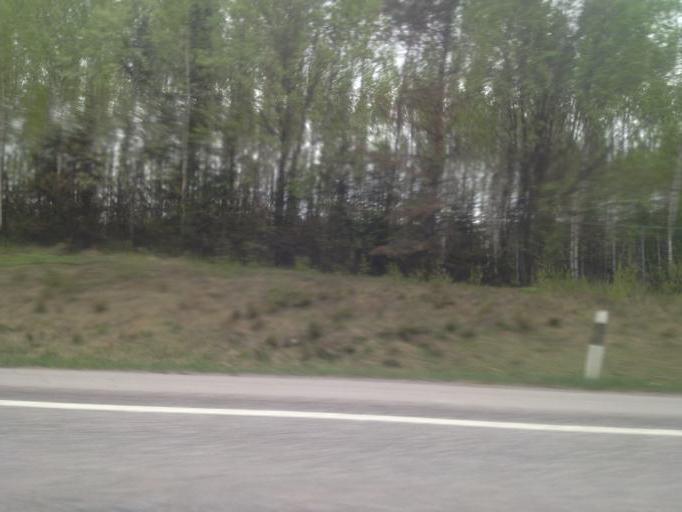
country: FI
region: Uusimaa
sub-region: Helsinki
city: Nurmijaervi
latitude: 60.4406
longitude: 24.8370
